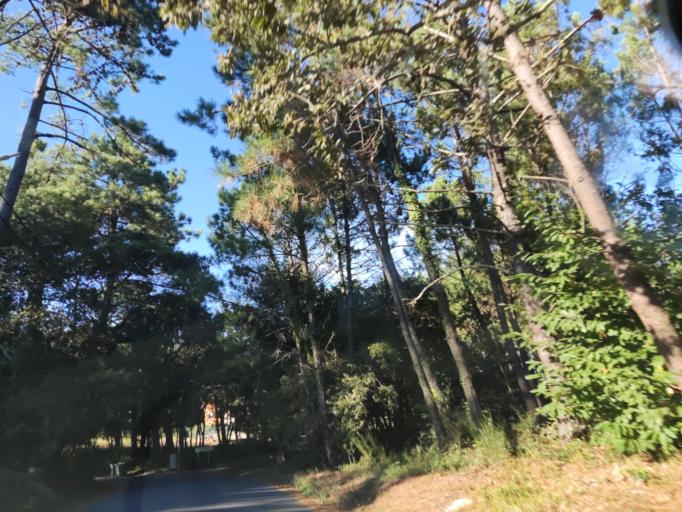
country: ES
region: Galicia
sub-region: Provincia da Coruna
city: Boiro
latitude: 42.5898
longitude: -8.9254
